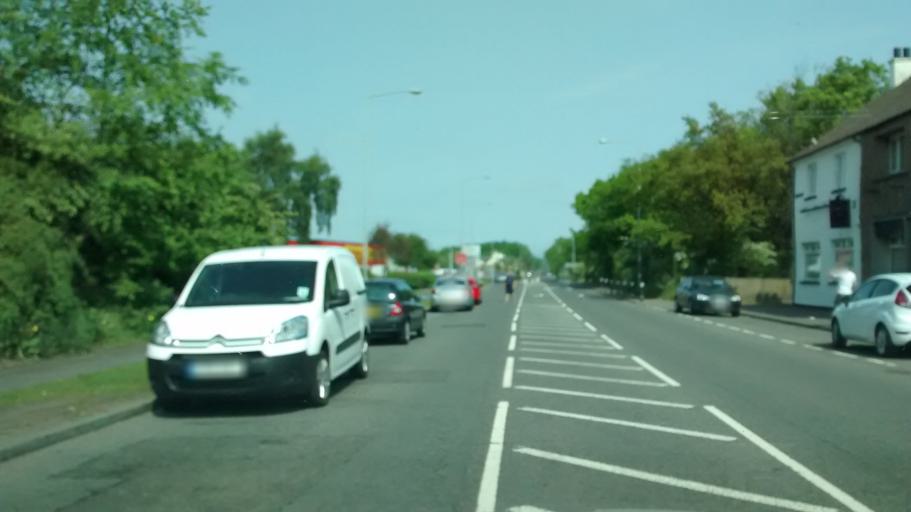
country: GB
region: Scotland
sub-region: West Lothian
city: Mid Calder
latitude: 55.9096
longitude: -3.4957
